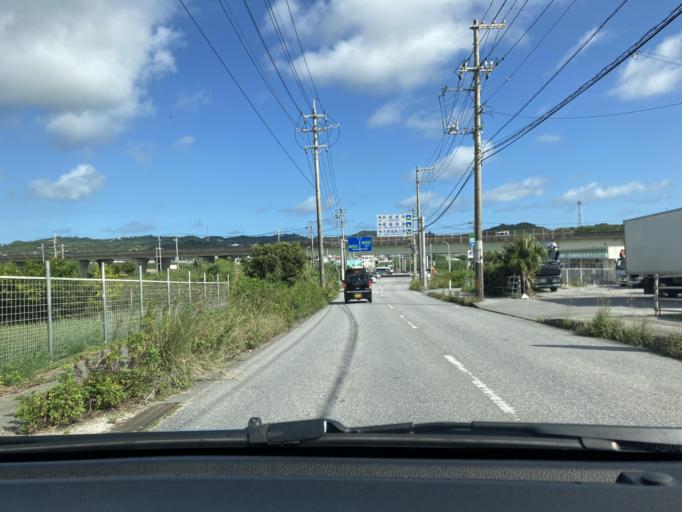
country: JP
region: Okinawa
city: Tomigusuku
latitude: 26.1841
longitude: 127.7330
